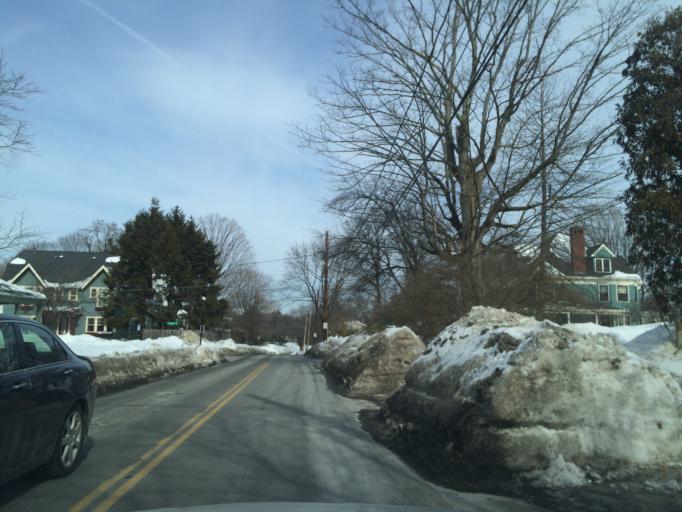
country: US
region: Massachusetts
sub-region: Middlesex County
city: Waltham
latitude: 42.3443
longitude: -71.2474
